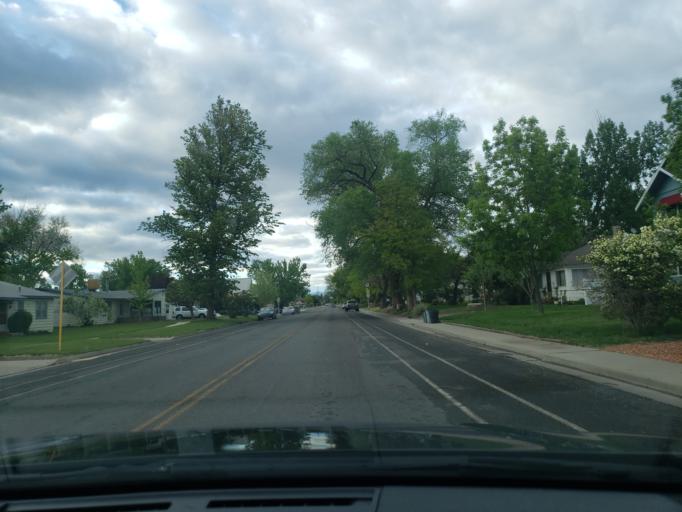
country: US
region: Colorado
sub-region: Mesa County
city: Fruita
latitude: 39.1610
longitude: -108.7336
